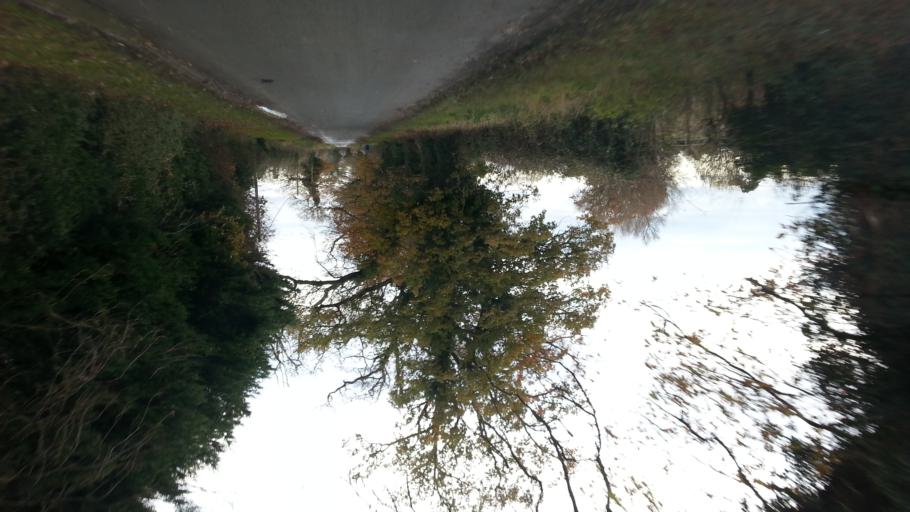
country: GB
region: England
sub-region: Suffolk
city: Ixworth
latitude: 52.3428
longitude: 0.8541
